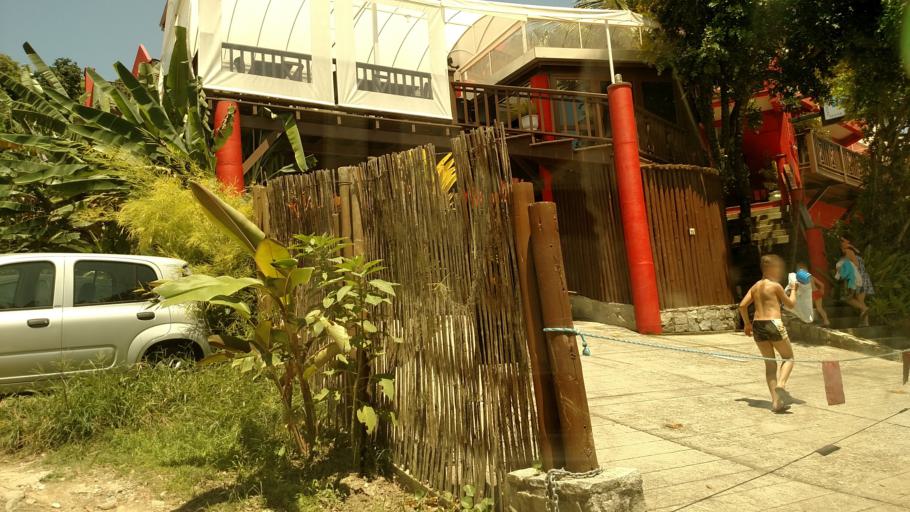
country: BR
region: Santa Catarina
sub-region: Porto Belo
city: Porto Belo
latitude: -27.1467
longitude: -48.4806
